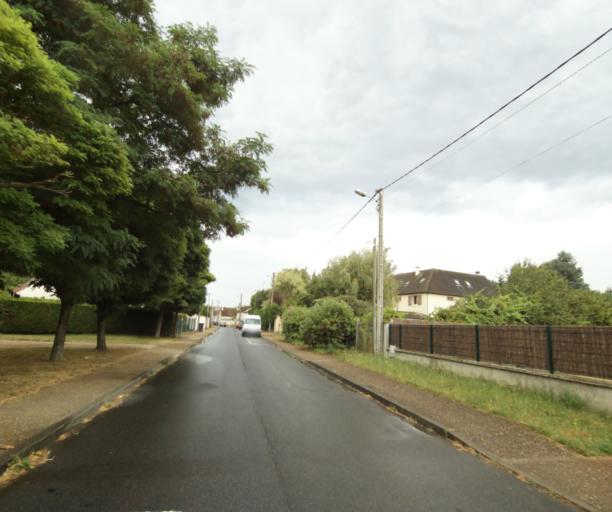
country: FR
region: Ile-de-France
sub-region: Departement de Seine-et-Marne
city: Perthes
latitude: 48.4804
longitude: 2.5495
